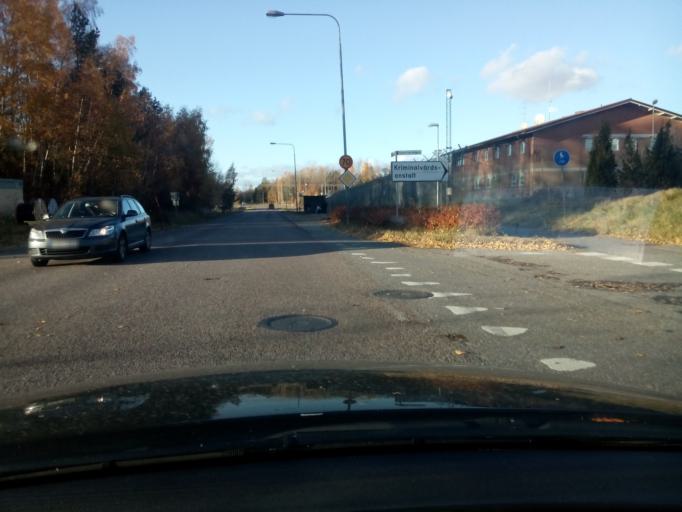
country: SE
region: Soedermanland
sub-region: Nykopings Kommun
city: Nykoping
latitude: 58.7219
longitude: 17.0229
